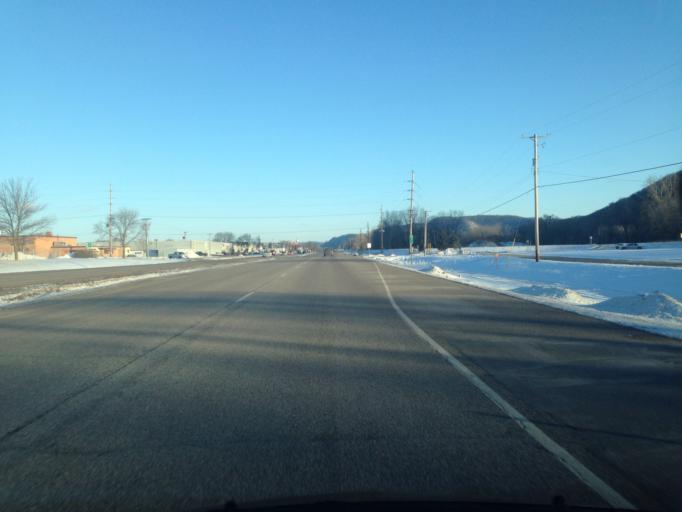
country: US
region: Minnesota
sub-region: Winona County
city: Goodview
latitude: 44.0653
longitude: -91.7152
